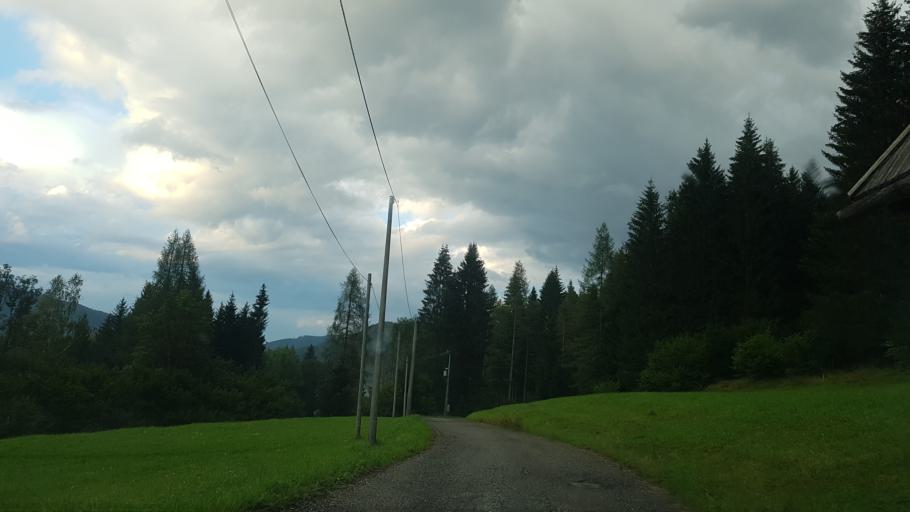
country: IT
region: Friuli Venezia Giulia
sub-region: Provincia di Udine
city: Tarvisio
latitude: 46.4869
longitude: 13.6189
